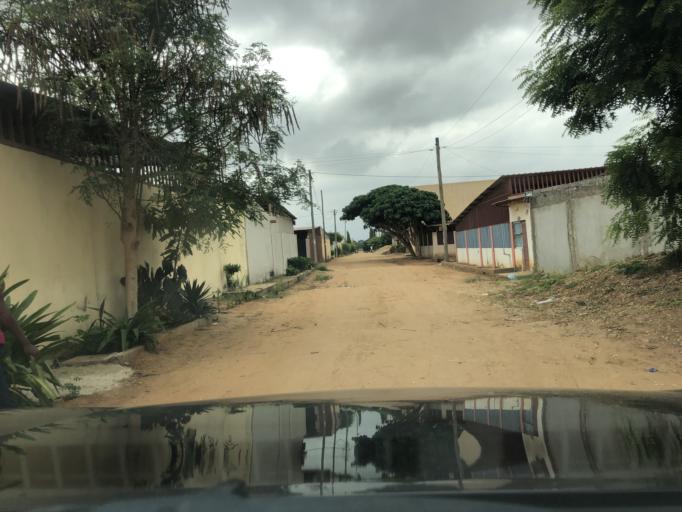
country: AO
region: Luanda
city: Luanda
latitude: -8.9369
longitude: 13.2523
